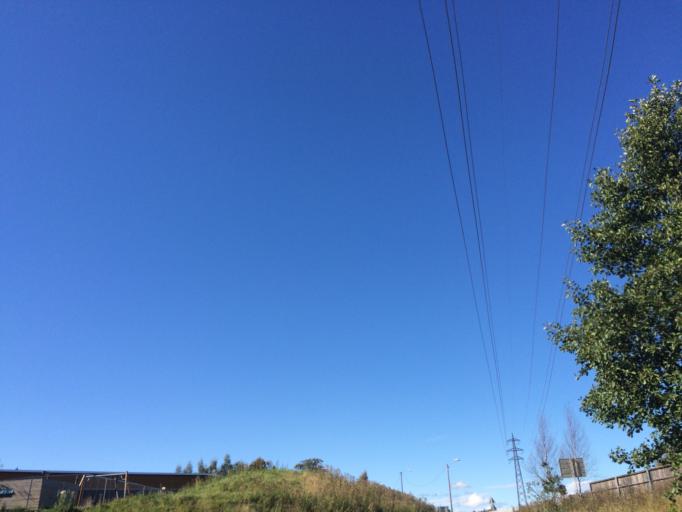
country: NO
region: Akershus
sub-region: Ski
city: Ski
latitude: 59.7195
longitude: 10.7950
